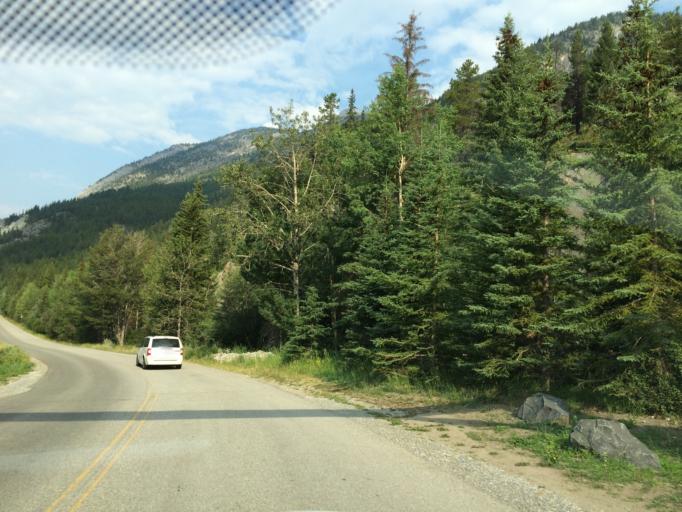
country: CA
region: Alberta
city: Banff
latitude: 51.1713
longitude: -115.6611
